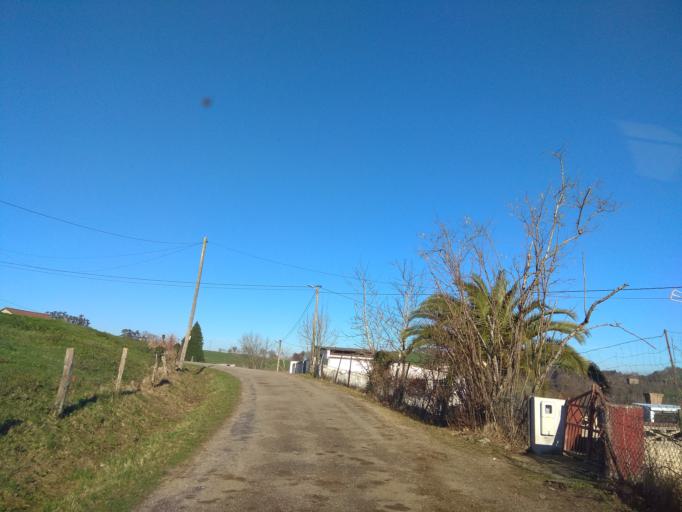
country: ES
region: Cantabria
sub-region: Provincia de Cantabria
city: Entrambasaguas
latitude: 43.3680
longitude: -3.6611
